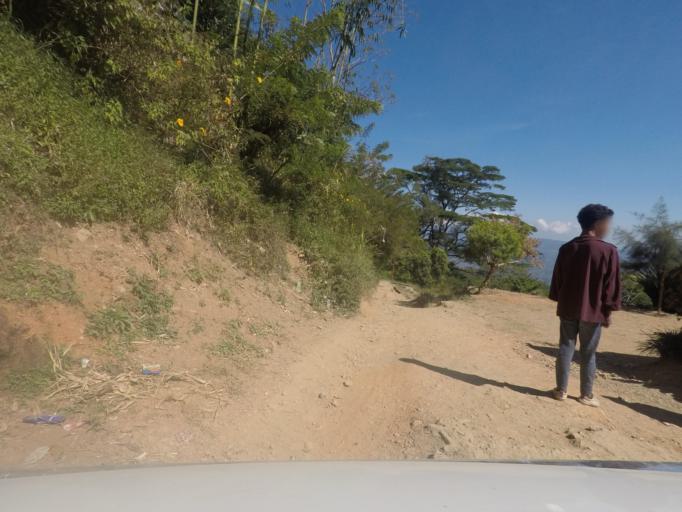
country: TL
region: Ermera
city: Gleno
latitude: -8.7237
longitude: 125.3300
